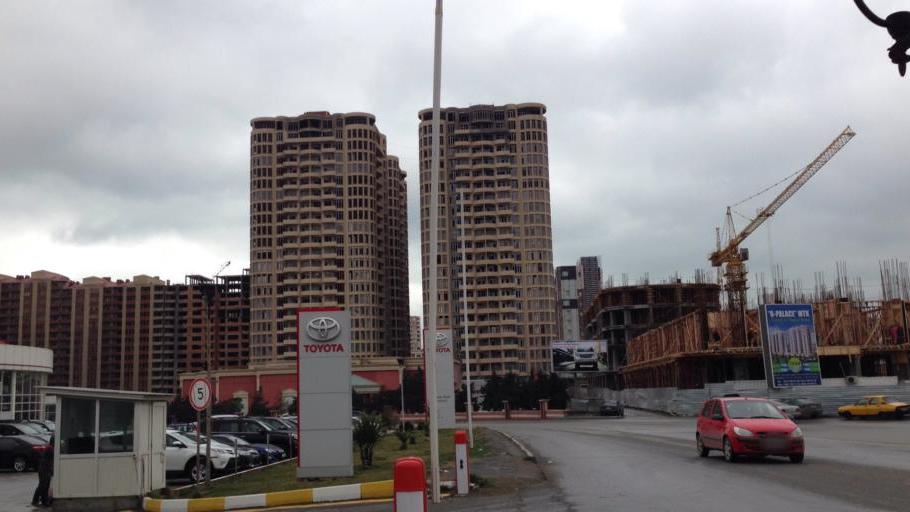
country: AZ
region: Baki
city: Baku
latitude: 40.3865
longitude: 49.8667
